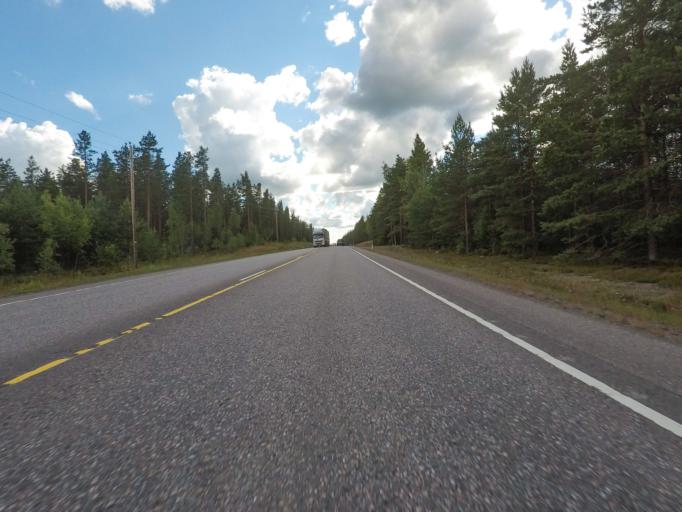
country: FI
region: Uusimaa
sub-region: Helsinki
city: Nurmijaervi
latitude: 60.5120
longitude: 24.6388
